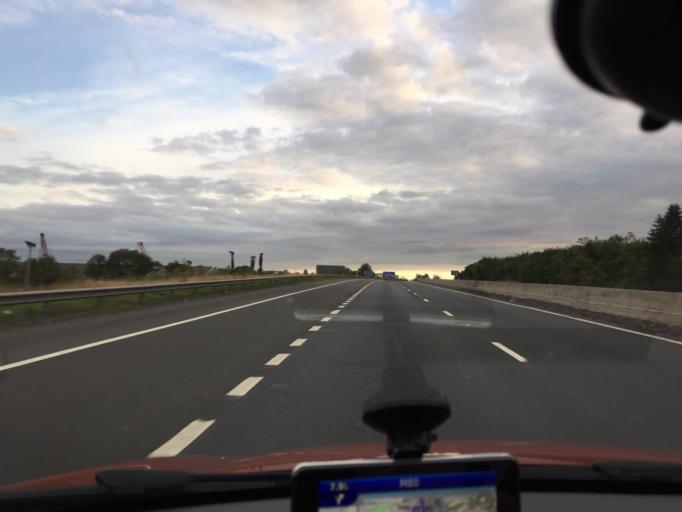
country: GB
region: Scotland
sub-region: North Lanarkshire
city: Cumbernauld
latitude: 55.9722
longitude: -3.9579
